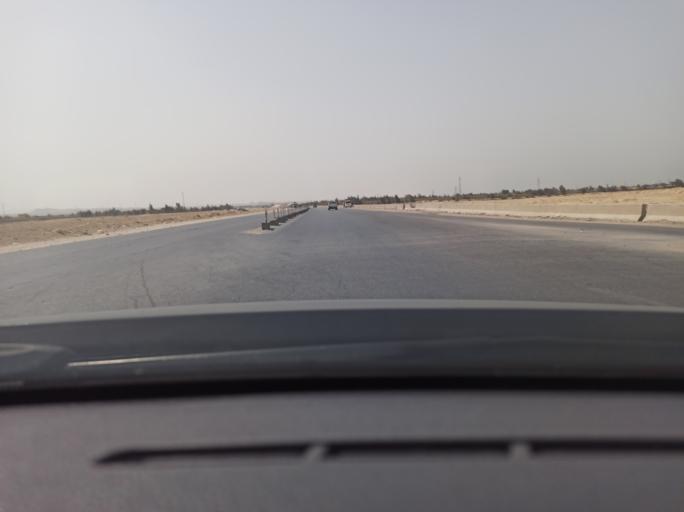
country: EG
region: Muhafazat al Fayyum
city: Al Wasitah
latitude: 29.2793
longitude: 31.2674
